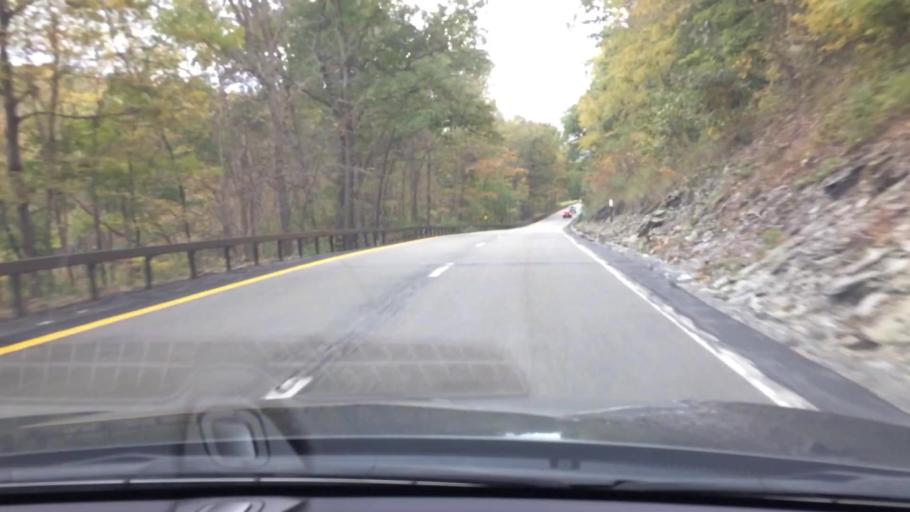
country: US
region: New York
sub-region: Dutchess County
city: Hillside Lake
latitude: 41.6156
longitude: -73.7629
